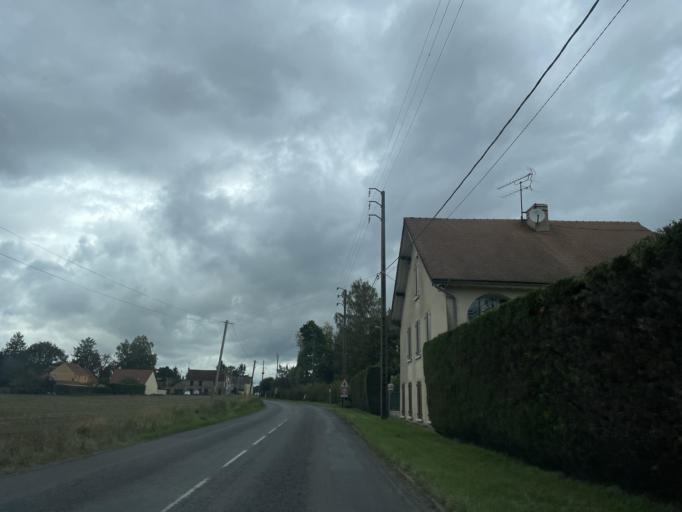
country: FR
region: Ile-de-France
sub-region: Departement de Seine-et-Marne
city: Sammeron
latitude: 48.8962
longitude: 3.0610
